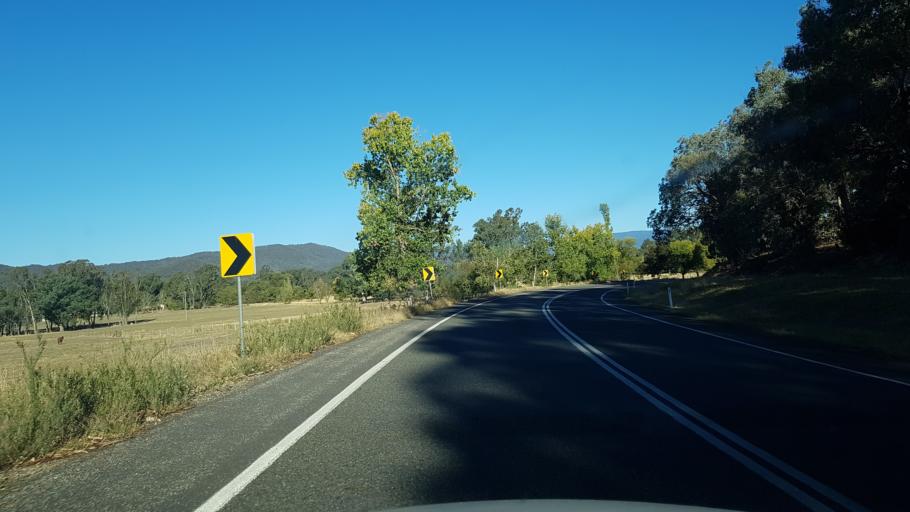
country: AU
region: Victoria
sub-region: Wangaratta
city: Wangaratta
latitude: -36.6247
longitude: 146.4053
